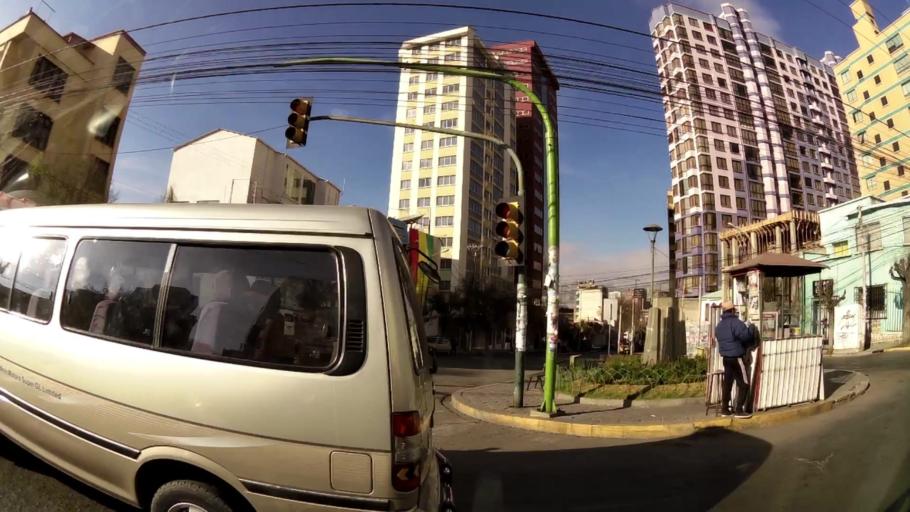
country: BO
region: La Paz
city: La Paz
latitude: -16.5026
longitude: -68.1198
